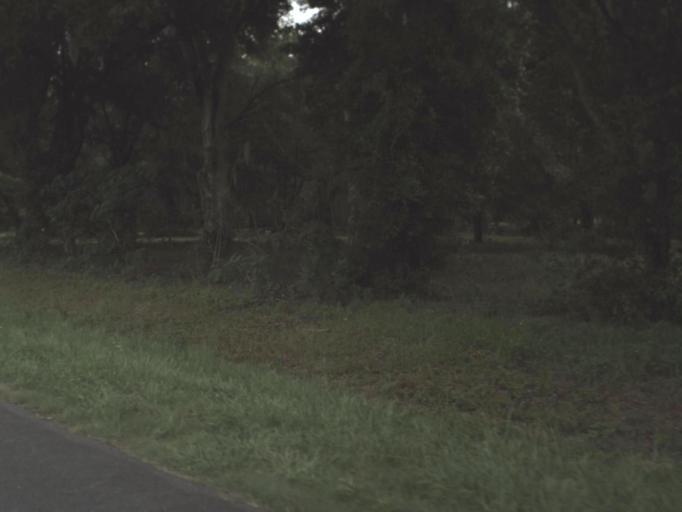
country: US
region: Florida
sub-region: Levy County
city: Williston Highlands
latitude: 29.2436
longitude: -82.4413
